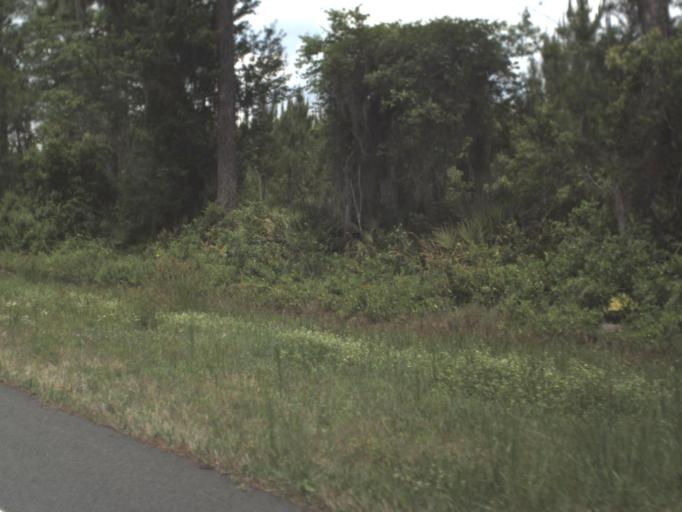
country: US
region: Florida
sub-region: Hamilton County
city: Jasper
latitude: 30.5918
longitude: -82.6777
